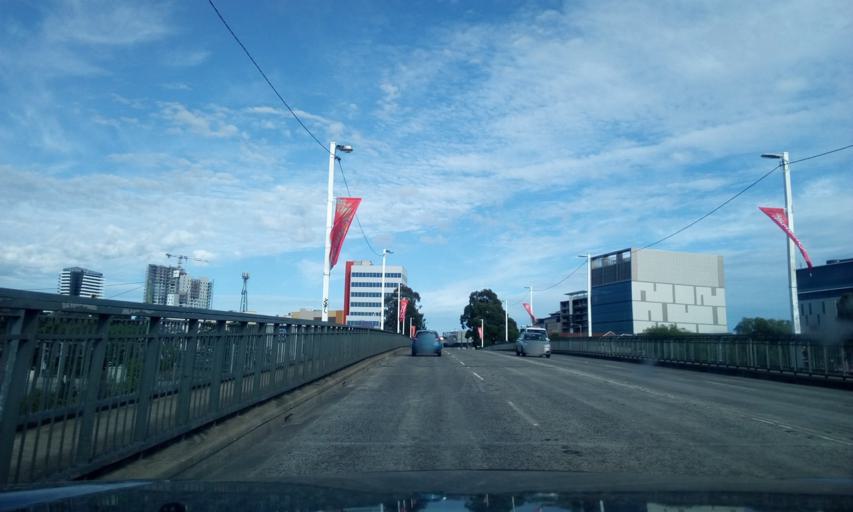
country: AU
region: New South Wales
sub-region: Fairfield
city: Liverpool
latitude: -33.9267
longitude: 150.9277
